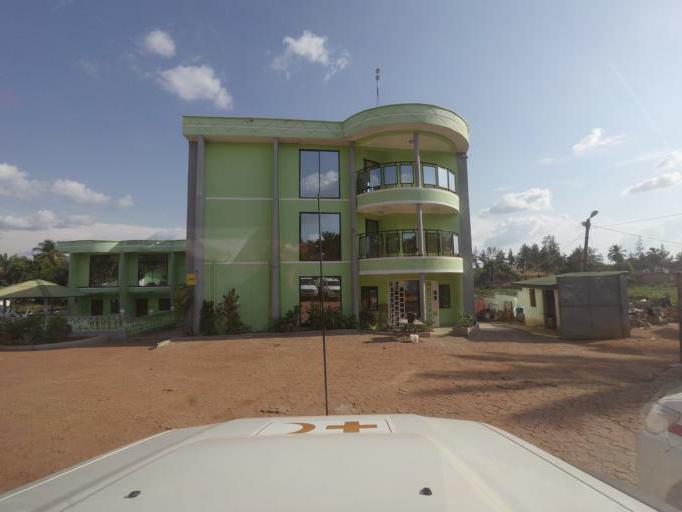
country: LR
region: Bong
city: Gbarnga
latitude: 7.0057
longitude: -9.4669
